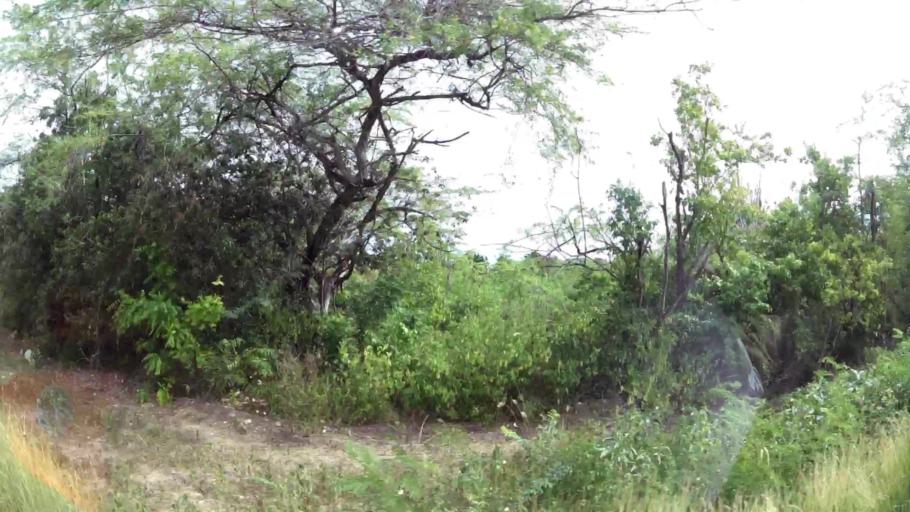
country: AG
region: Saint Paul
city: Falmouth
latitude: 17.0429
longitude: -61.6906
